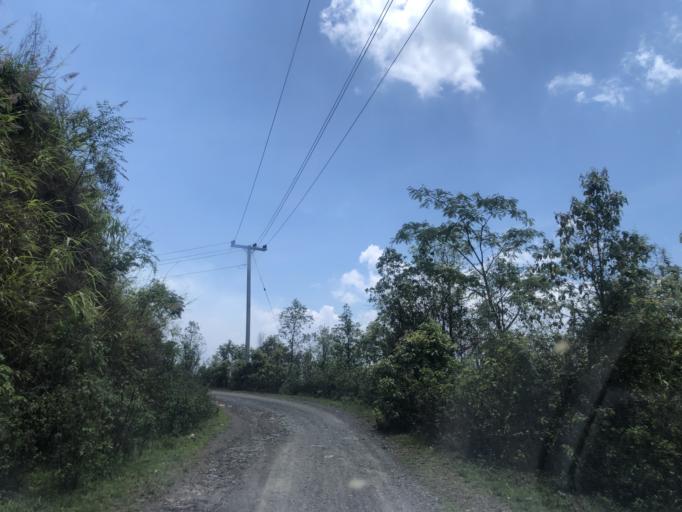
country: LA
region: Phongsali
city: Phongsali
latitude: 21.4368
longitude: 102.1614
